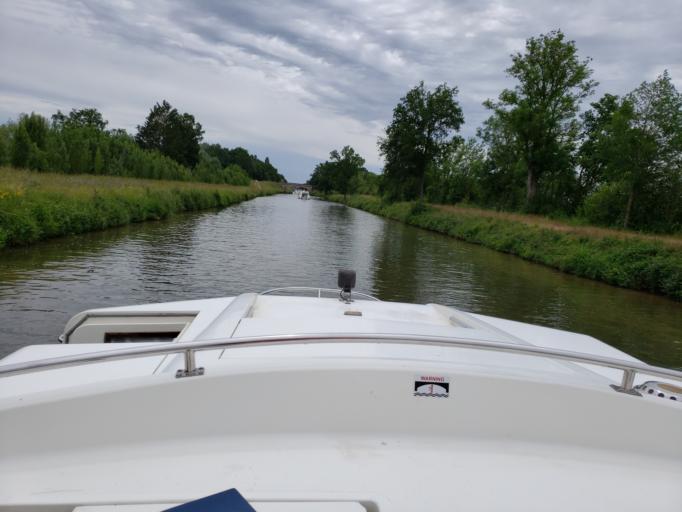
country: FR
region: Bourgogne
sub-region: Departement de l'Yonne
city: Appoigny
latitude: 47.8896
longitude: 3.5417
